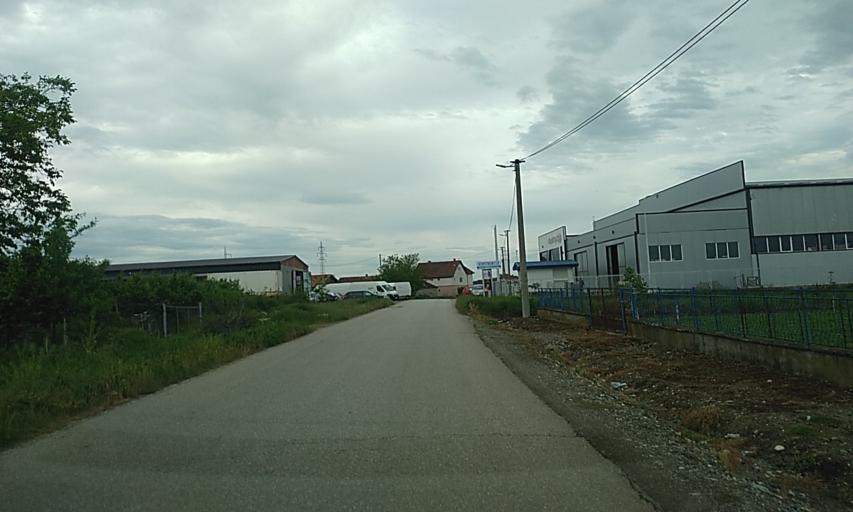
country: RS
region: Central Serbia
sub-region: Rasinski Okrug
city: Krusevac
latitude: 43.5910
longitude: 21.2818
